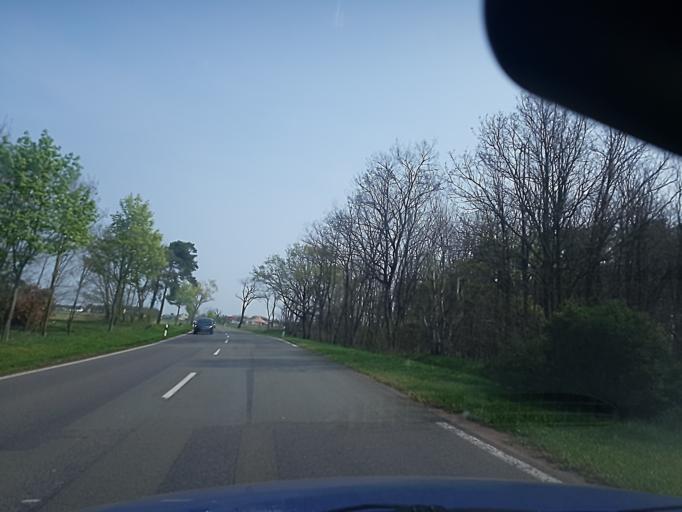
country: DE
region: Saxony
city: Beilrode
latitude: 51.5929
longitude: 13.1173
